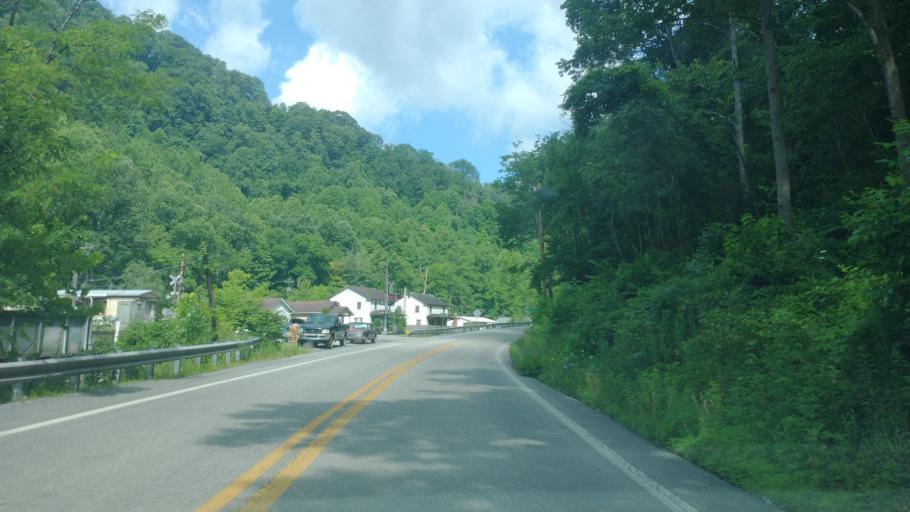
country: US
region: West Virginia
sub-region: McDowell County
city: Welch
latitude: 37.4142
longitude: -81.4824
